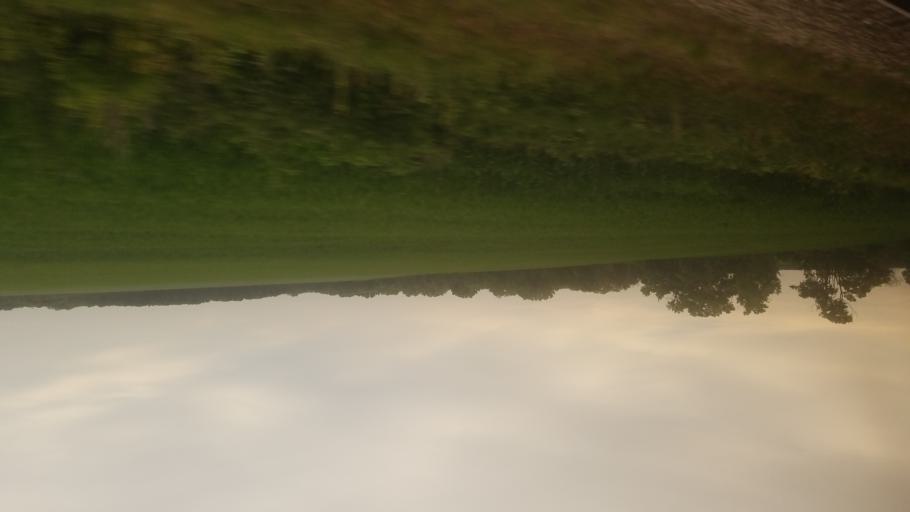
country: US
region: Kansas
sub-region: Chase County
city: Cottonwood Falls
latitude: 38.3888
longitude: -96.5226
